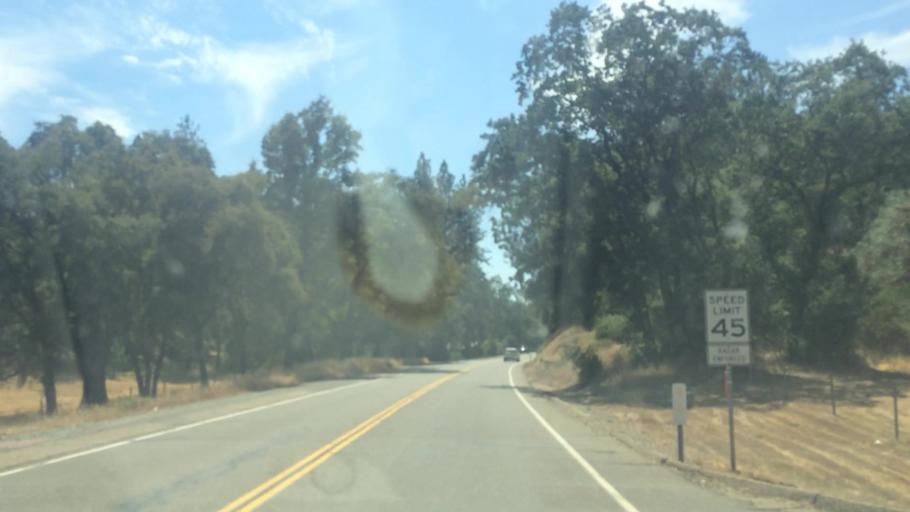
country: US
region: California
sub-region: Amador County
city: Pine Grove
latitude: 38.4029
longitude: -120.7230
